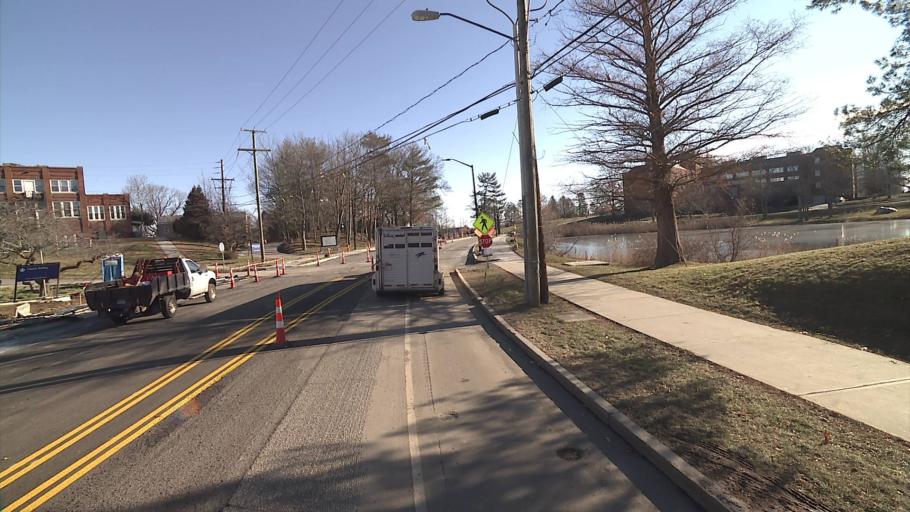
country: US
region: Connecticut
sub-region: Tolland County
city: Storrs
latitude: 41.8115
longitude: -72.2530
